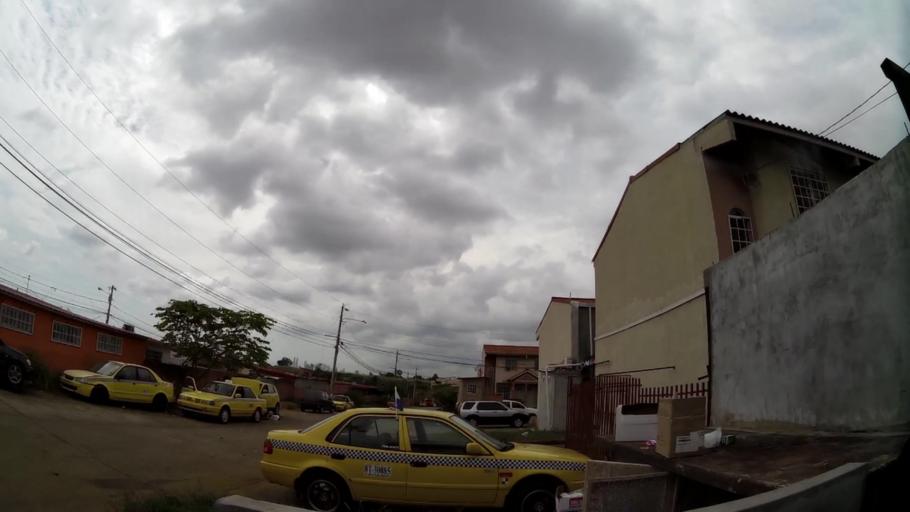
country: PA
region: Panama
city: San Miguelito
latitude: 9.0603
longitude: -79.4245
